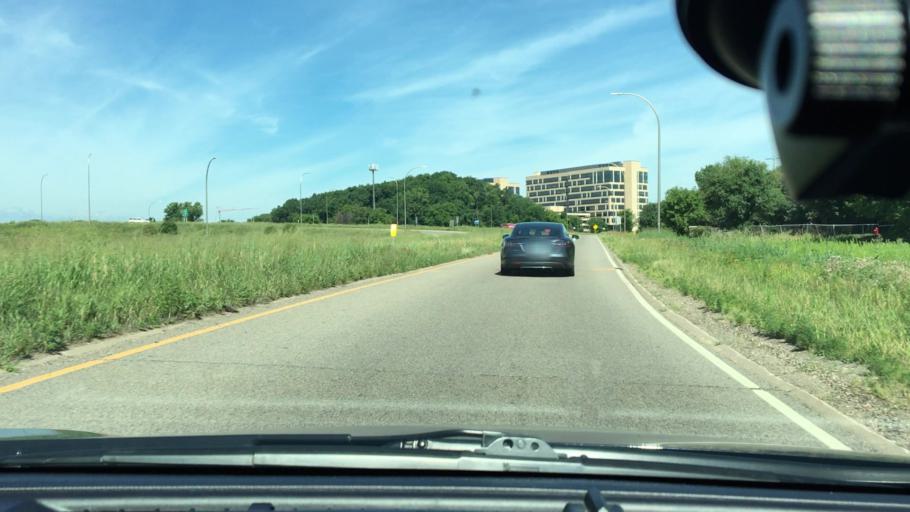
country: US
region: Minnesota
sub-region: Hennepin County
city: Edina
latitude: 44.8911
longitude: -93.3967
